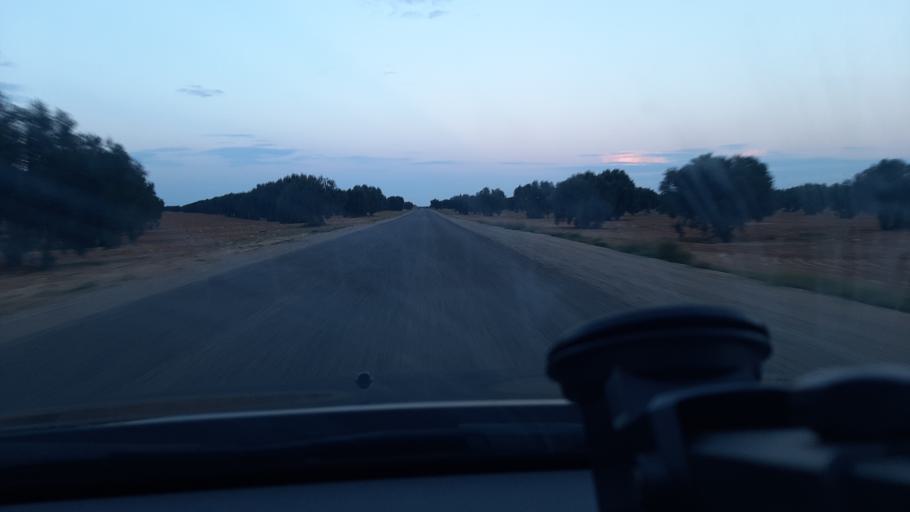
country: TN
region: Al Mahdiyah
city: Shurban
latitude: 34.9872
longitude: 10.3913
